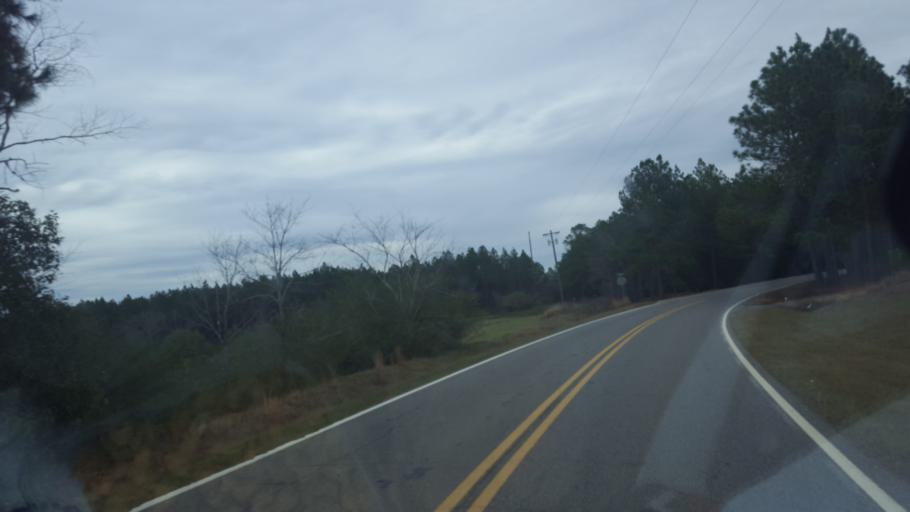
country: US
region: Georgia
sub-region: Ben Hill County
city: Fitzgerald
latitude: 31.7705
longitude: -83.3568
